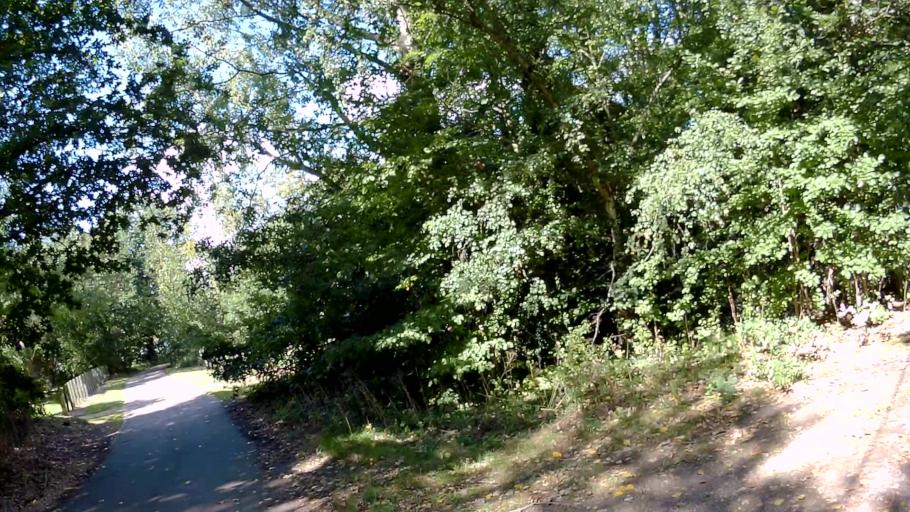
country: GB
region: England
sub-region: Bracknell Forest
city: Crowthorne
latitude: 51.3945
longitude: -0.7803
